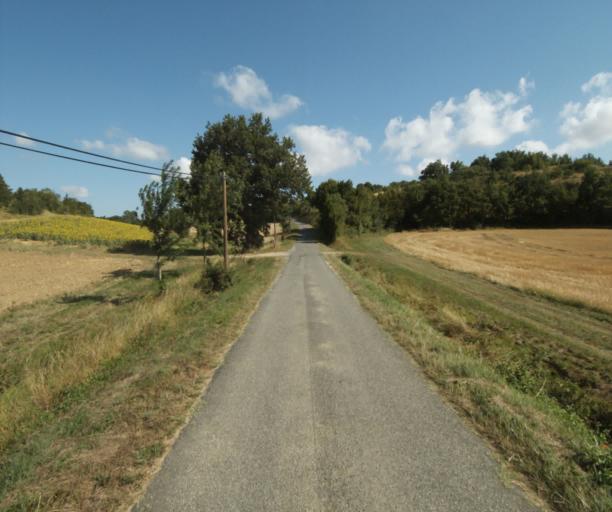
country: FR
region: Midi-Pyrenees
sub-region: Departement de la Haute-Garonne
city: Saint-Felix-Lauragais
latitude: 43.4485
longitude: 1.8284
